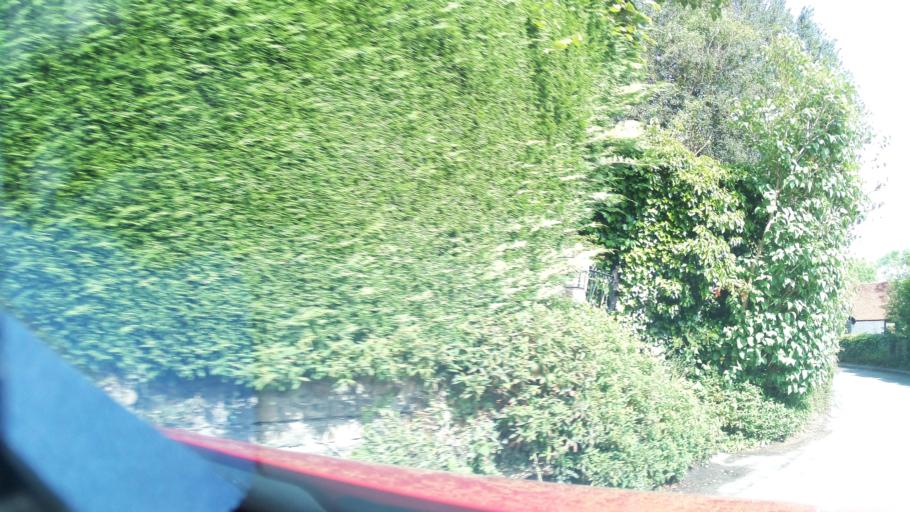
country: GB
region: England
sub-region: Hertfordshire
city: Chorleywood
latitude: 51.6543
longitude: -0.4767
